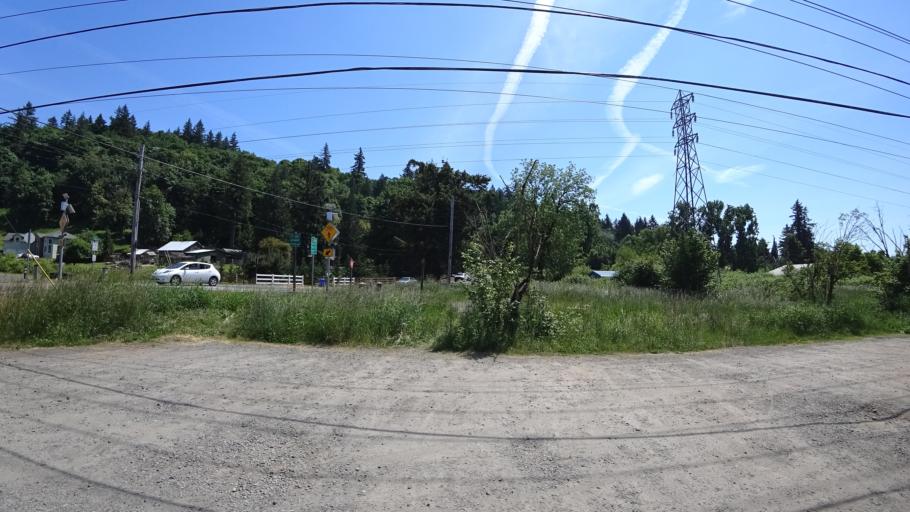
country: US
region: Oregon
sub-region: Multnomah County
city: Gresham
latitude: 45.4856
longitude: -122.4854
